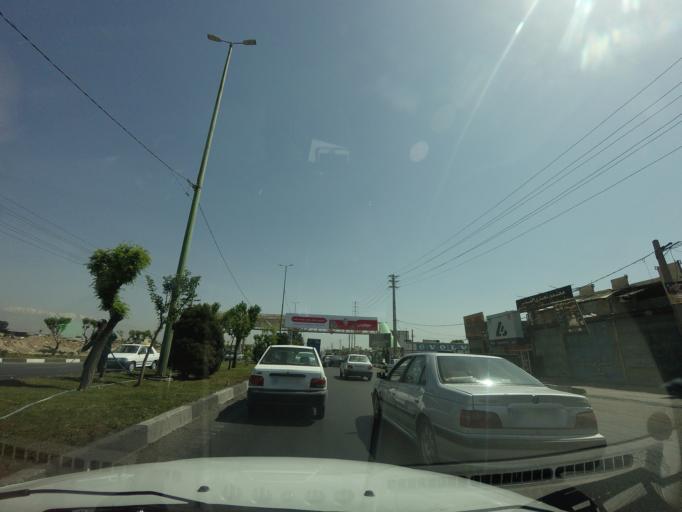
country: IR
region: Tehran
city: Eslamshahr
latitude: 35.5843
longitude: 51.2782
